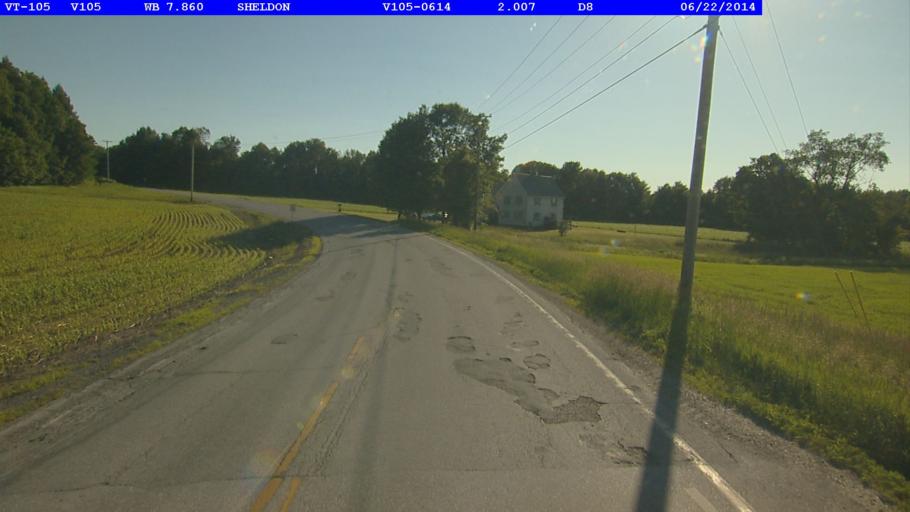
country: US
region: Vermont
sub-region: Franklin County
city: Saint Albans
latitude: 44.9047
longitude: -72.9922
